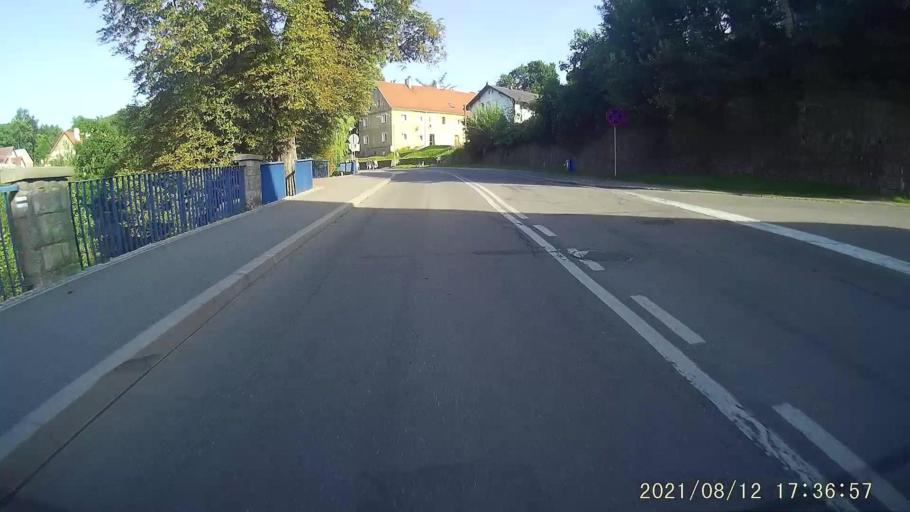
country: PL
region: Lower Silesian Voivodeship
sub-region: Powiat klodzki
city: Ladek-Zdroj
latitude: 50.3434
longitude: 16.8801
